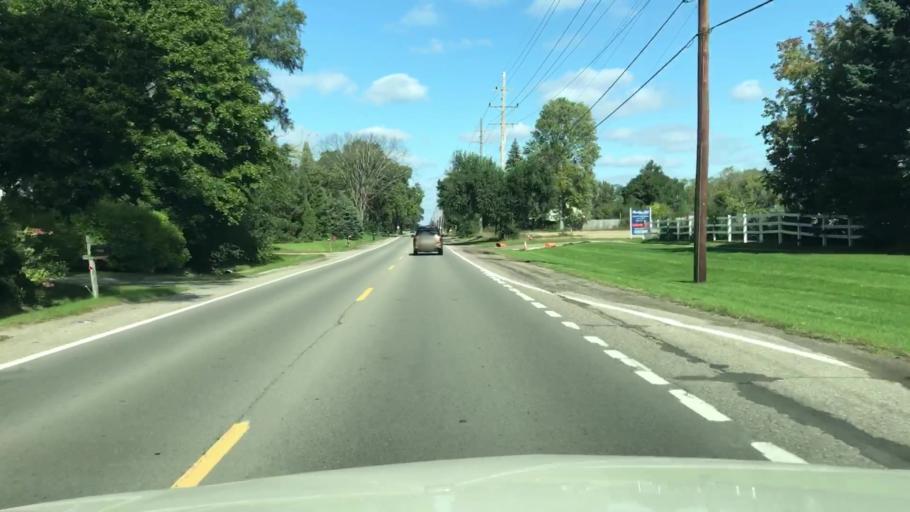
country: US
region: Michigan
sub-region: Oakland County
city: Rochester
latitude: 42.6441
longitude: -83.0924
